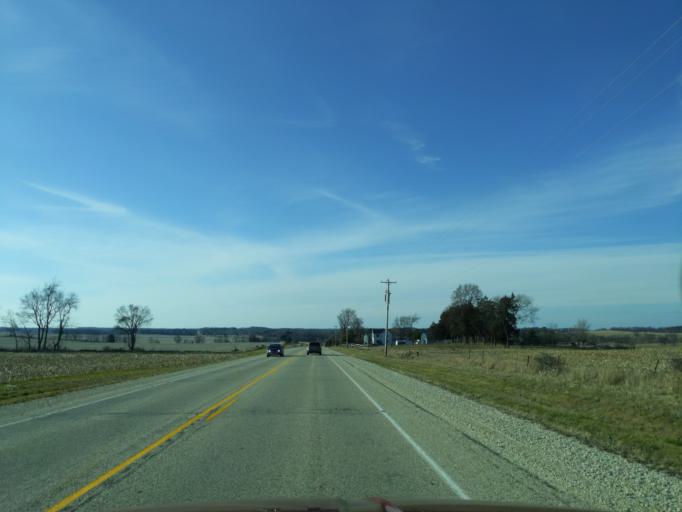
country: US
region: Wisconsin
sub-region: Jefferson County
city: Lake Koshkonong
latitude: 42.8297
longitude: -88.8597
